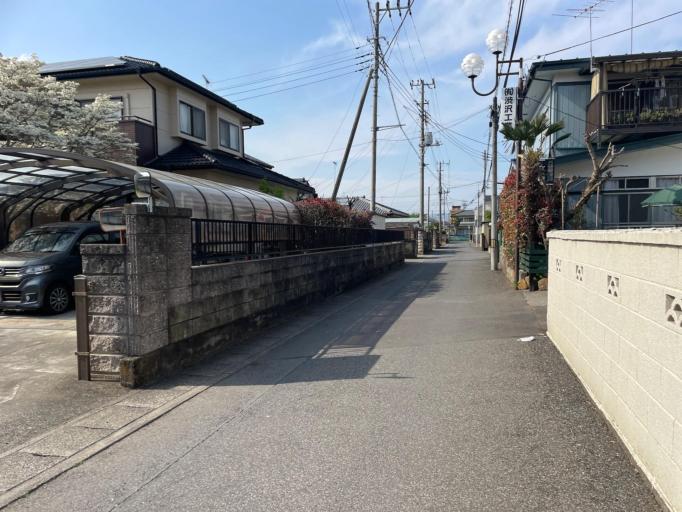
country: JP
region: Gunma
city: Ota
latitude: 36.3062
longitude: 139.4046
